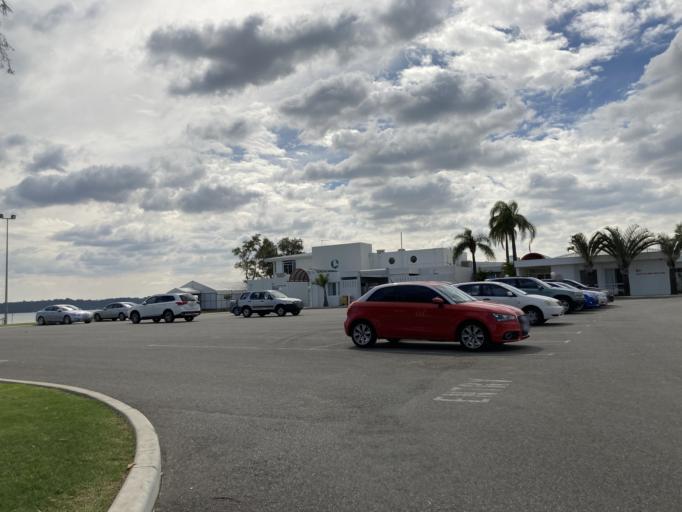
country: AU
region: Western Australia
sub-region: Melville
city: Applecross
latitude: -32.0028
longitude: 115.8456
